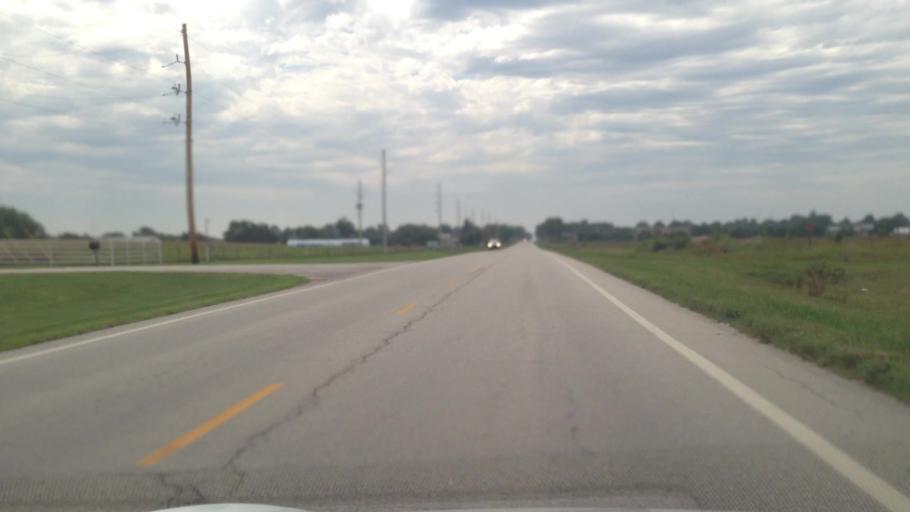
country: US
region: Kansas
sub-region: Allen County
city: Iola
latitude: 37.9286
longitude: -95.1701
